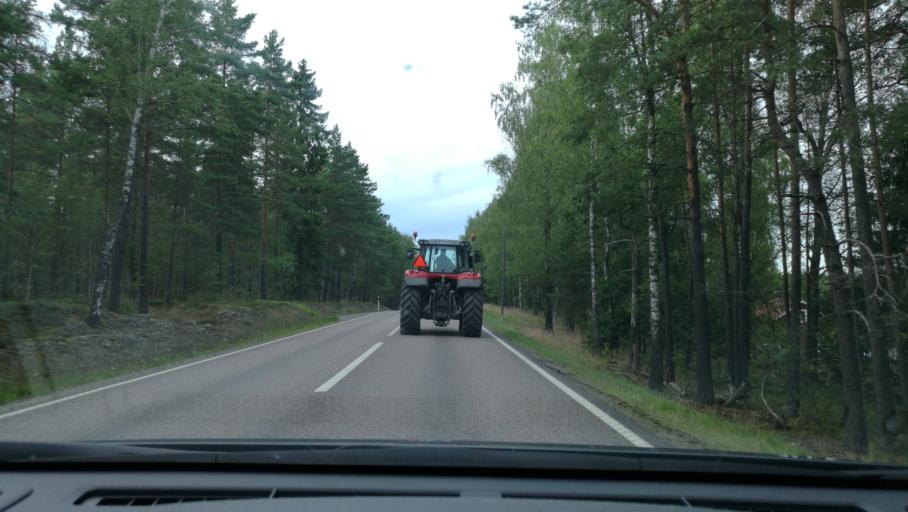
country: SE
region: Vaestmanland
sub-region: Kungsors Kommun
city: Kungsoer
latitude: 59.3332
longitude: 16.1117
